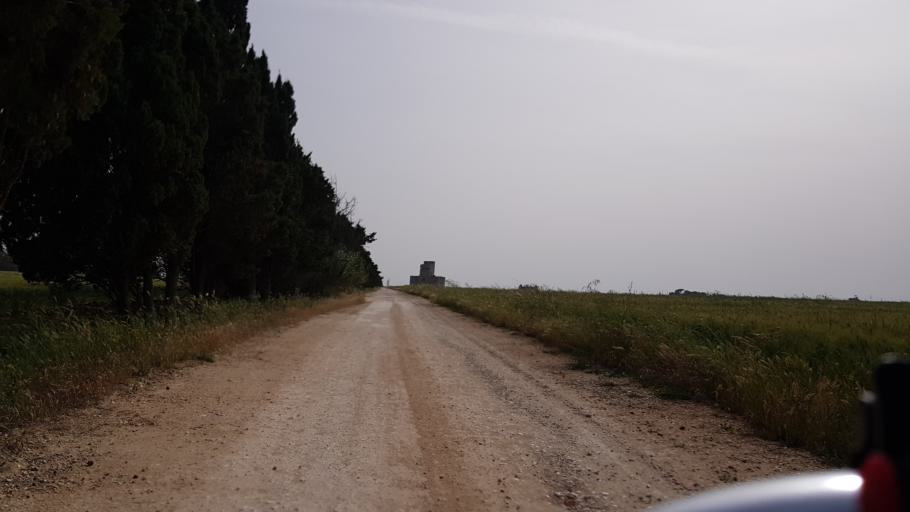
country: IT
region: Apulia
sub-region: Provincia di Brindisi
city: La Rosa
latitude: 40.5995
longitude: 18.0248
